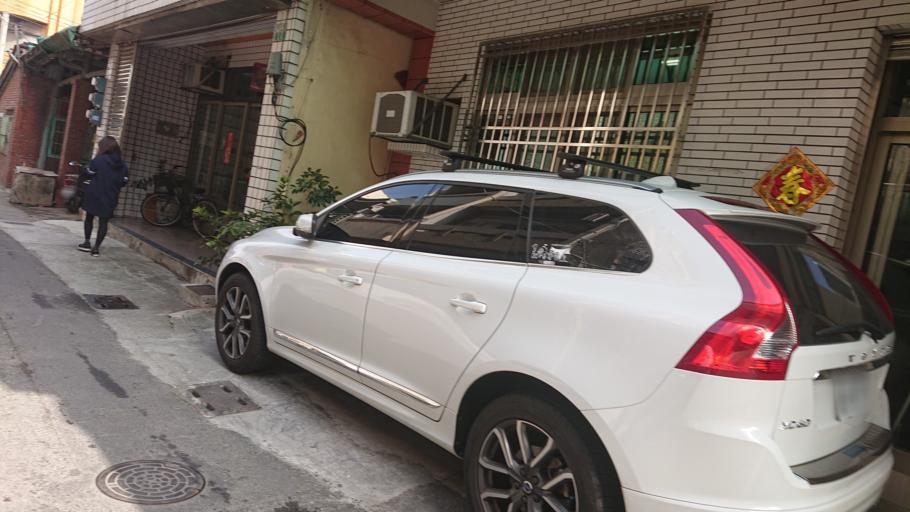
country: TW
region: Taiwan
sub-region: Chiayi
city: Taibao
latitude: 23.4674
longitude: 120.2444
